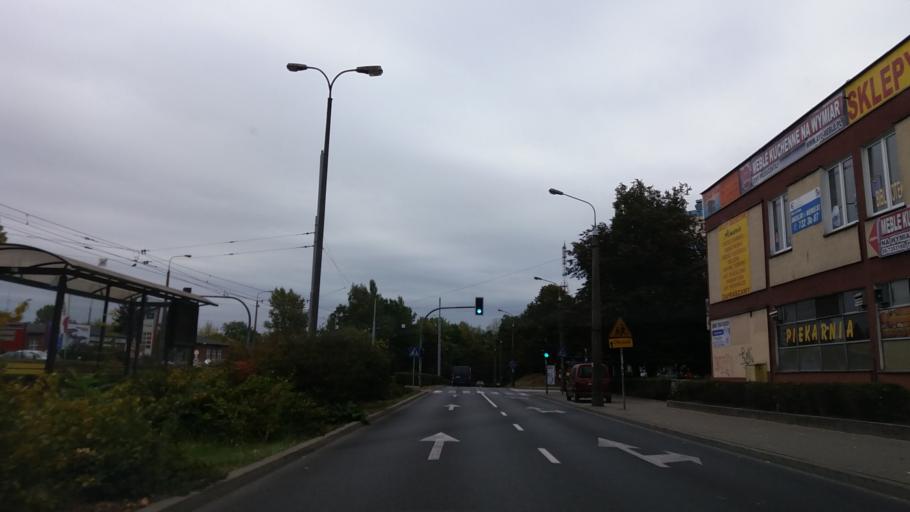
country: PL
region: Lubusz
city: Gorzow Wielkopolski
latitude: 52.7419
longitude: 15.2533
